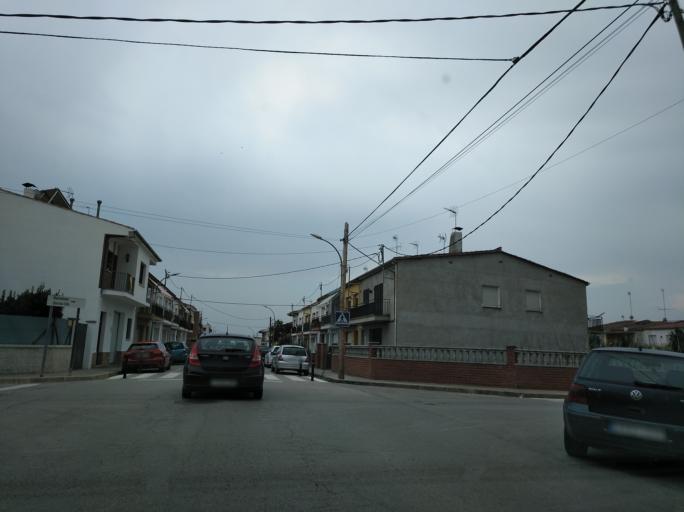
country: ES
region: Catalonia
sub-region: Provincia de Girona
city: Santa Coloma de Farners
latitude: 41.8578
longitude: 2.6698
